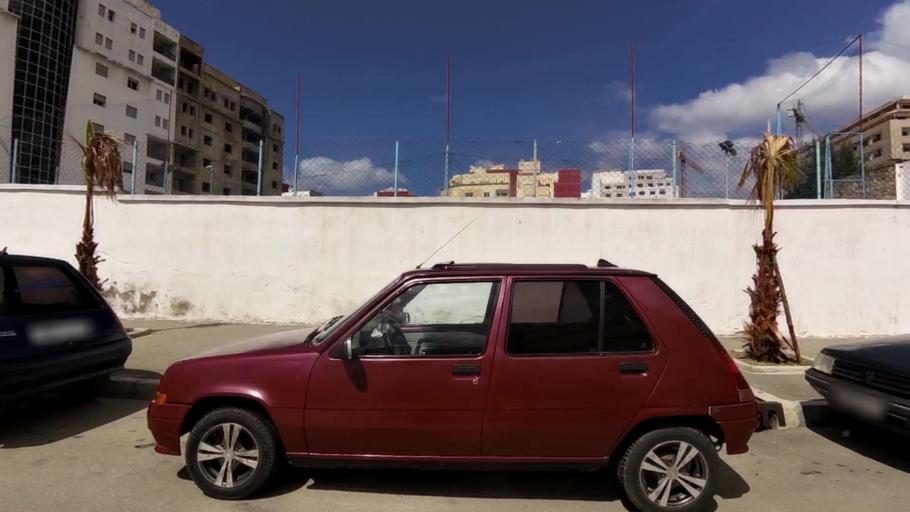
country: MA
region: Tanger-Tetouan
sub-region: Tanger-Assilah
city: Tangier
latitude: 35.7674
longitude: -5.8103
